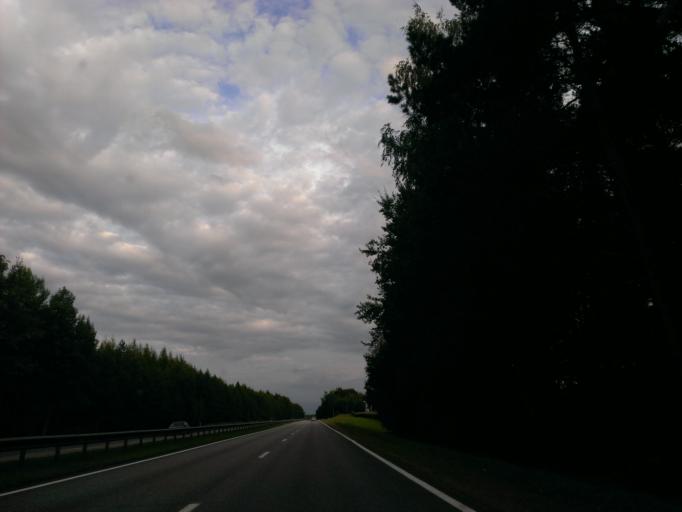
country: LV
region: Ikskile
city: Ikskile
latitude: 56.8302
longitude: 24.5147
